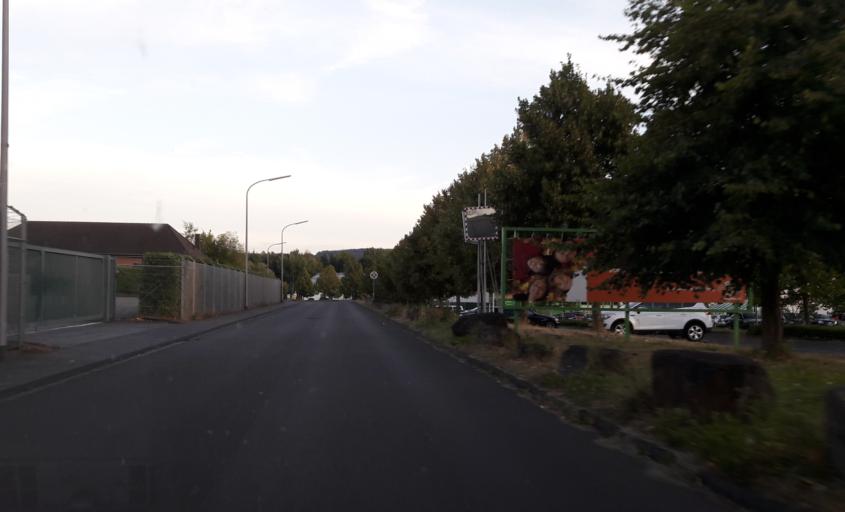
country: DE
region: Rheinland-Pfalz
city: Briedel
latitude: 50.0275
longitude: 7.1579
